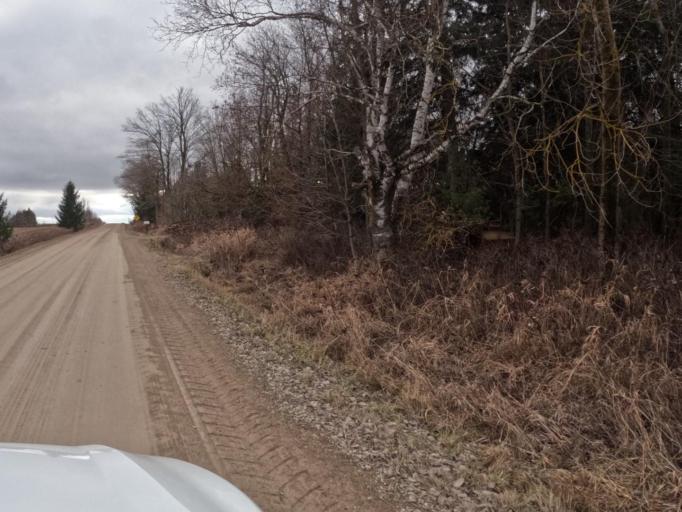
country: CA
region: Ontario
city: Shelburne
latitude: 43.8752
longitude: -80.3798
